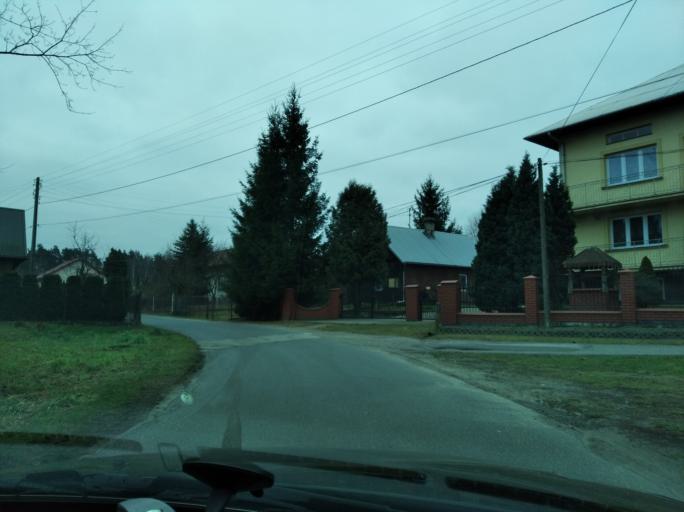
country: PL
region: Subcarpathian Voivodeship
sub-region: Powiat lancucki
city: Rakszawa
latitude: 50.1554
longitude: 22.2309
